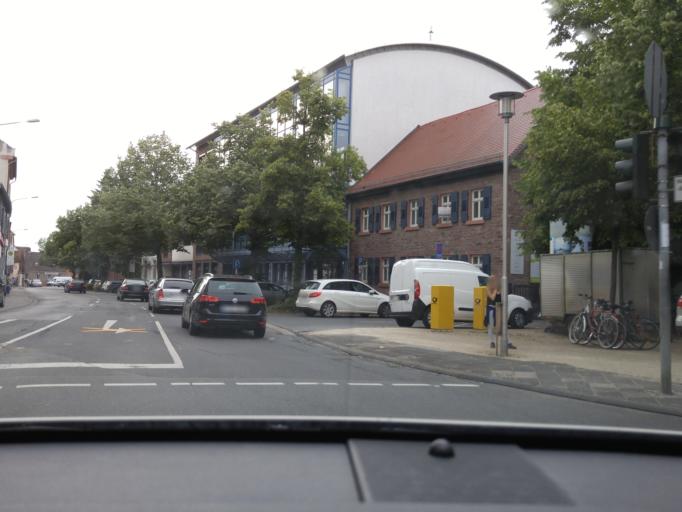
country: DE
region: Hesse
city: Langen
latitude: 49.9872
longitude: 8.6790
